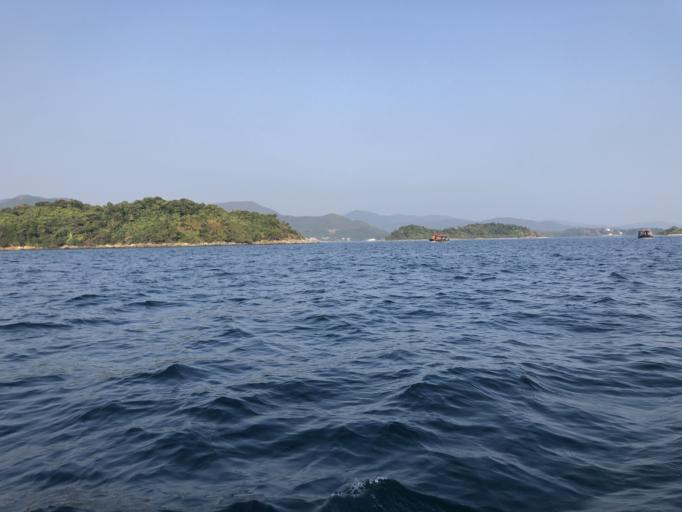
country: HK
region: Sai Kung
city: Sai Kung
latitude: 22.3771
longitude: 114.2792
